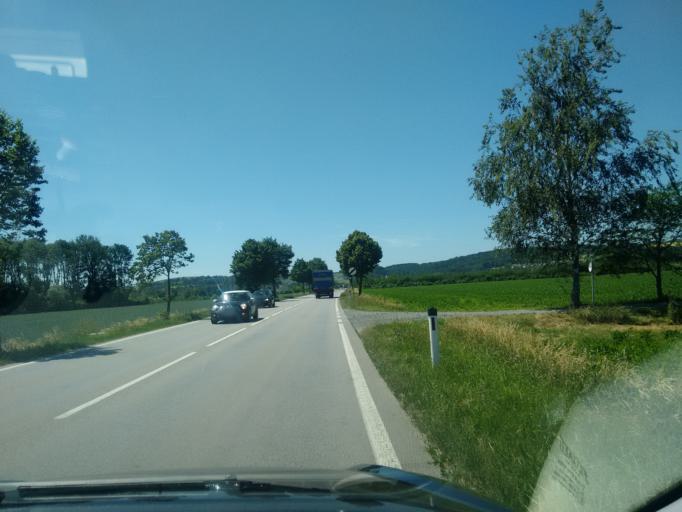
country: AT
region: Lower Austria
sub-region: Politischer Bezirk Sankt Polten
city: Hafnerbach
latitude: 48.1976
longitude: 15.4792
